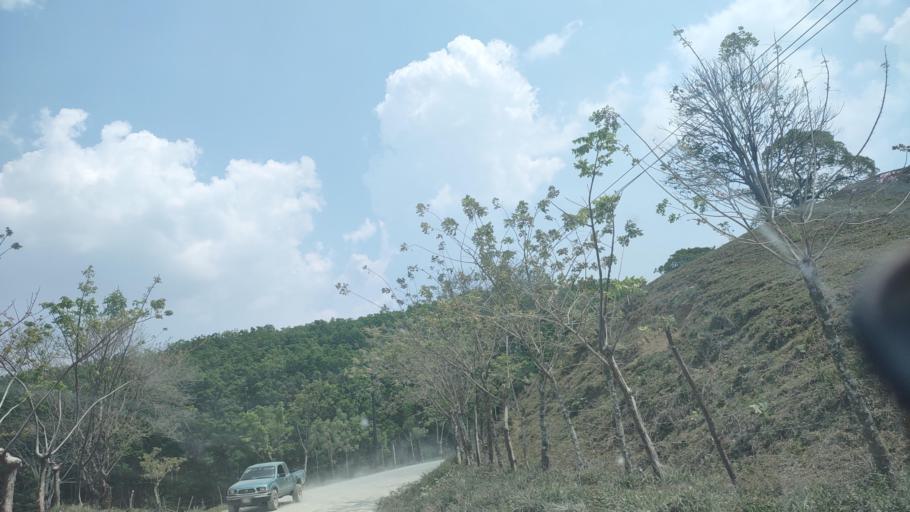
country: MX
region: Tabasco
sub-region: Huimanguillo
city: Francisco Rueda
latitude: 17.6055
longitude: -93.9058
